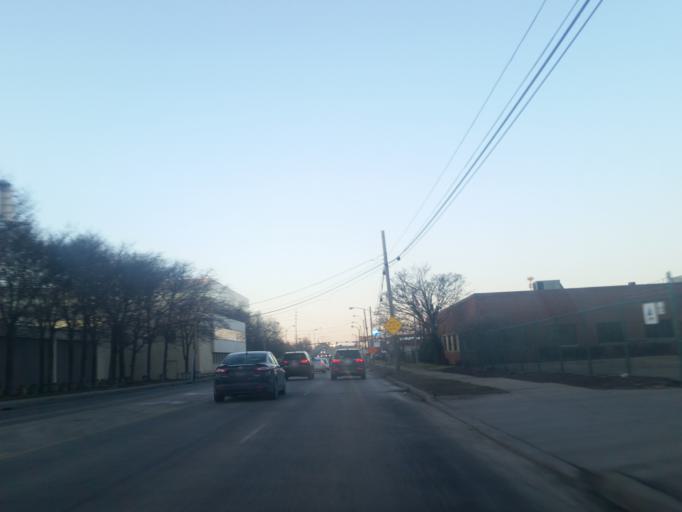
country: US
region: Ohio
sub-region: Cuyahoga County
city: Lakewood
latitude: 41.4418
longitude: -81.8012
